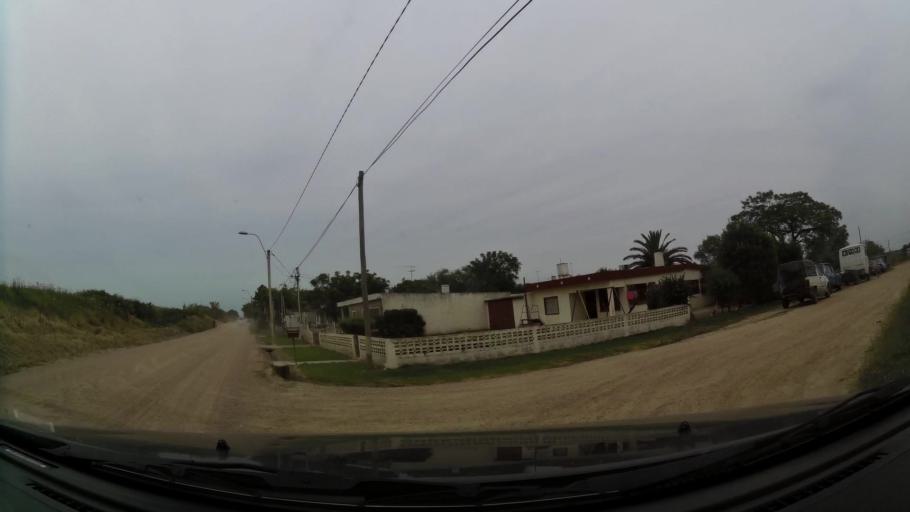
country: UY
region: Canelones
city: La Paz
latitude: -34.7474
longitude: -56.2333
